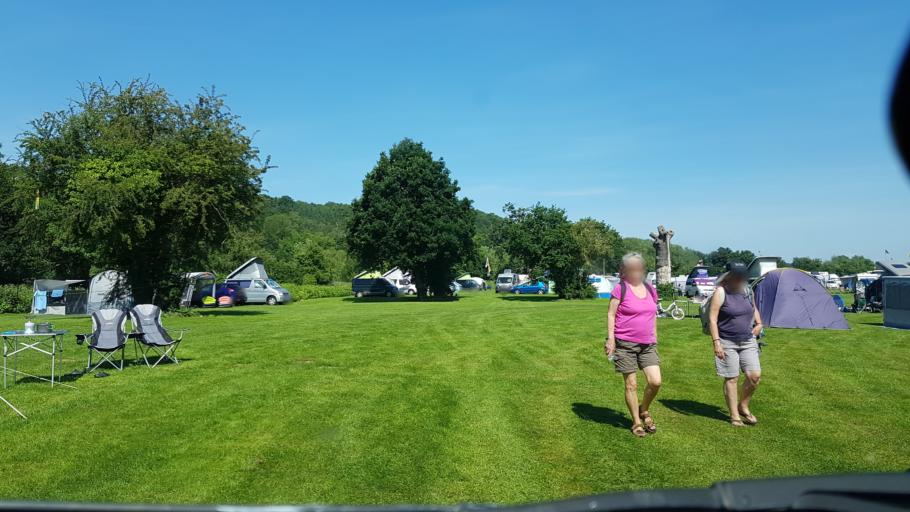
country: GB
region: England
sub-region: Worcestershire
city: Stourport-on-Severn
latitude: 52.3420
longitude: -2.2997
